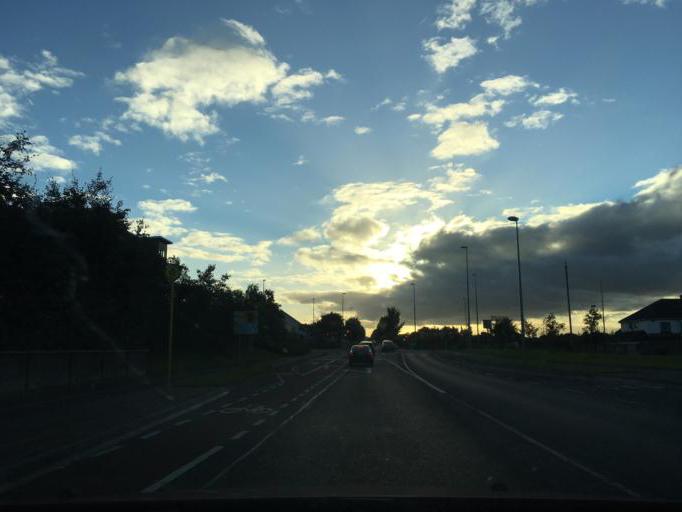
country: IE
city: Knocklyon
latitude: 53.2768
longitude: -6.3294
